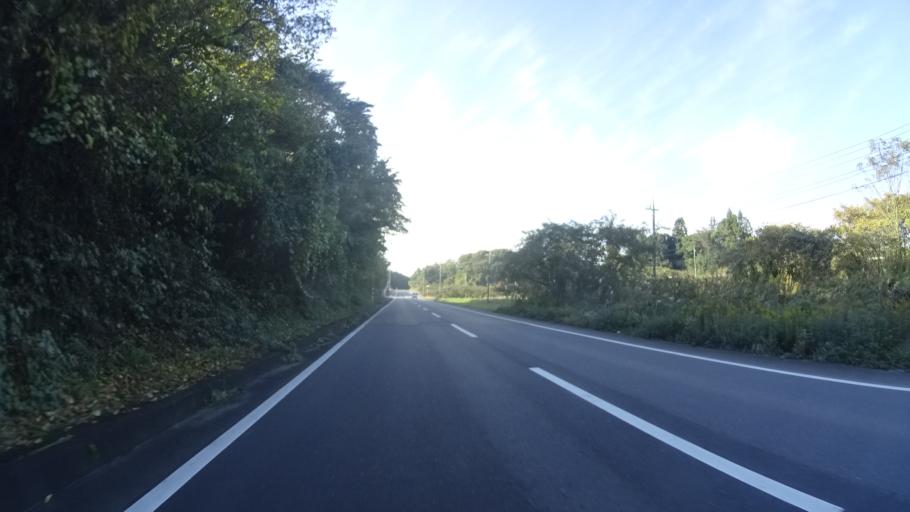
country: JP
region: Ishikawa
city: Hakui
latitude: 37.0048
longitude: 136.8060
